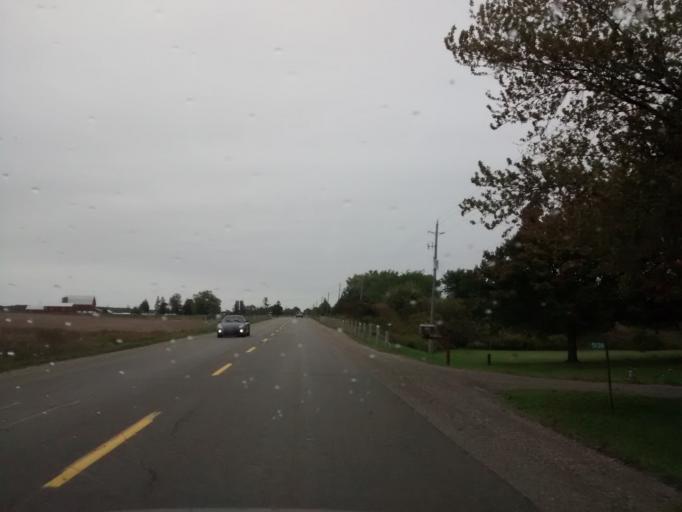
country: CA
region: Ontario
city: Hamilton
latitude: 42.8526
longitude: -79.8198
